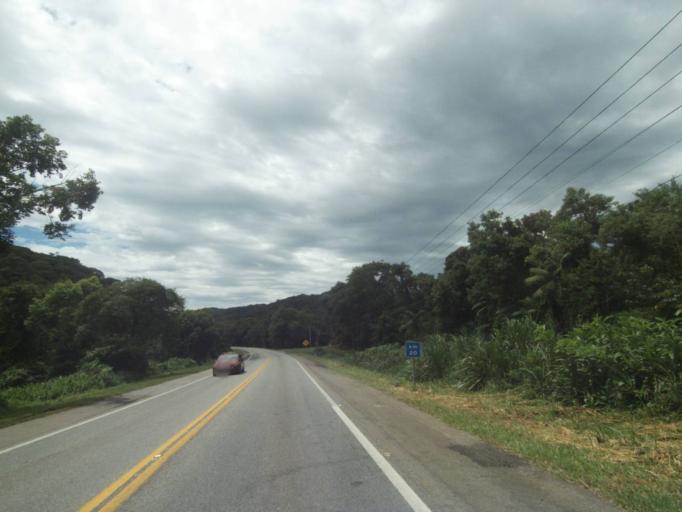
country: BR
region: Parana
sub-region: Antonina
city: Antonina
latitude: -25.4480
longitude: -48.7785
